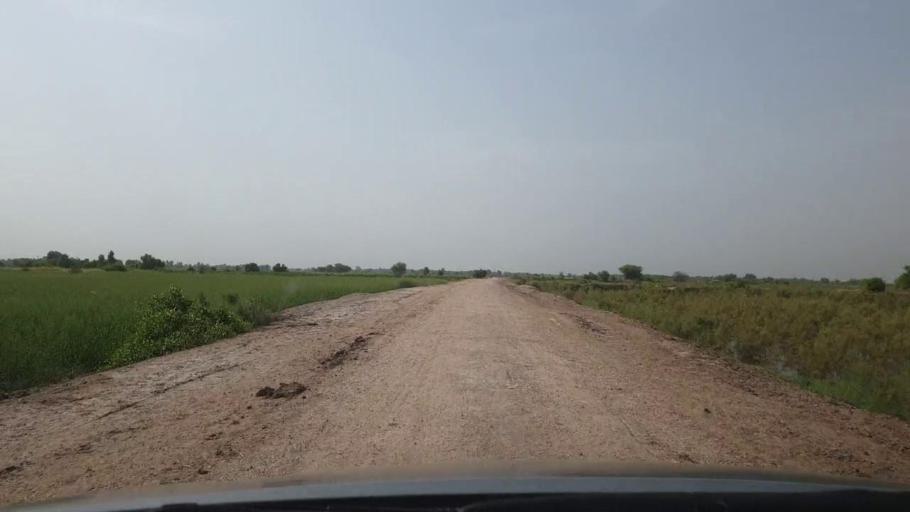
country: PK
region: Sindh
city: Rohri
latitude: 27.6738
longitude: 69.0127
